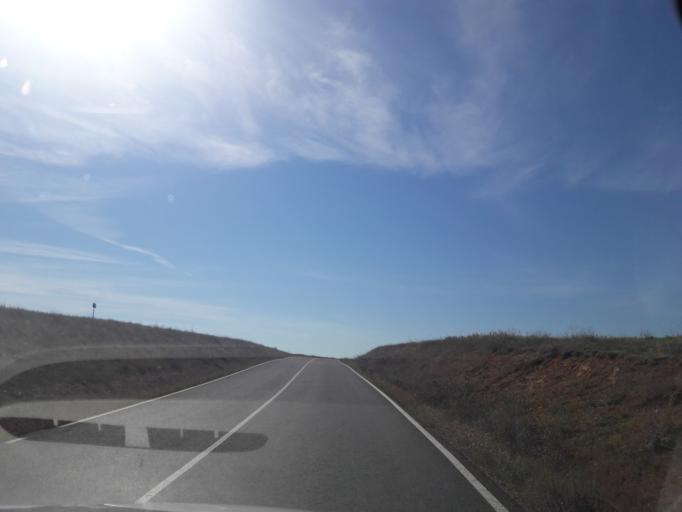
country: ES
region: Castille and Leon
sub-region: Provincia de Salamanca
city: Espino de la Orbada
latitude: 41.0880
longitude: -5.4098
